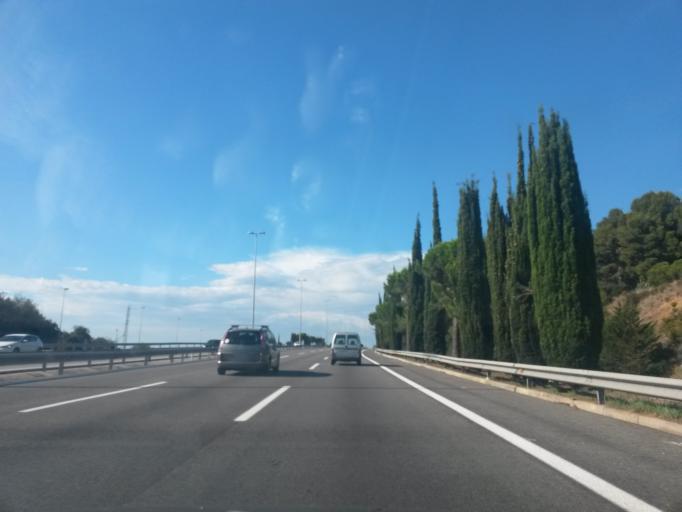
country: ES
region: Catalonia
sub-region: Provincia de Barcelona
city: Cabrera de Mar
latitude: 41.5287
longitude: 2.4124
